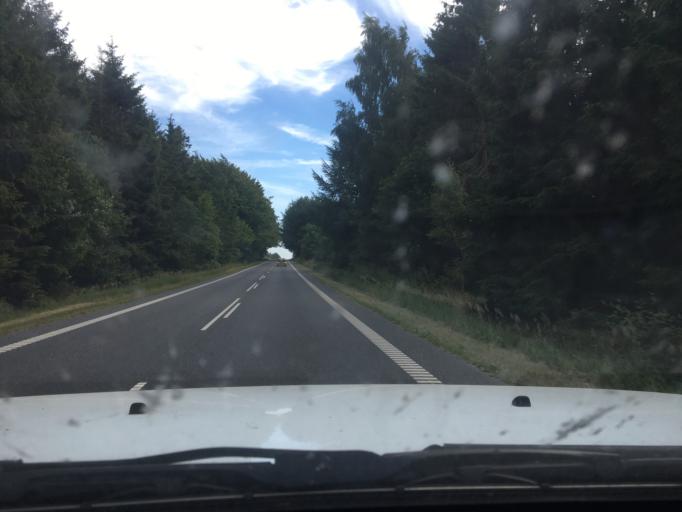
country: DK
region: Central Jutland
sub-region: Viborg Kommune
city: Viborg
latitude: 56.6085
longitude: 9.3544
